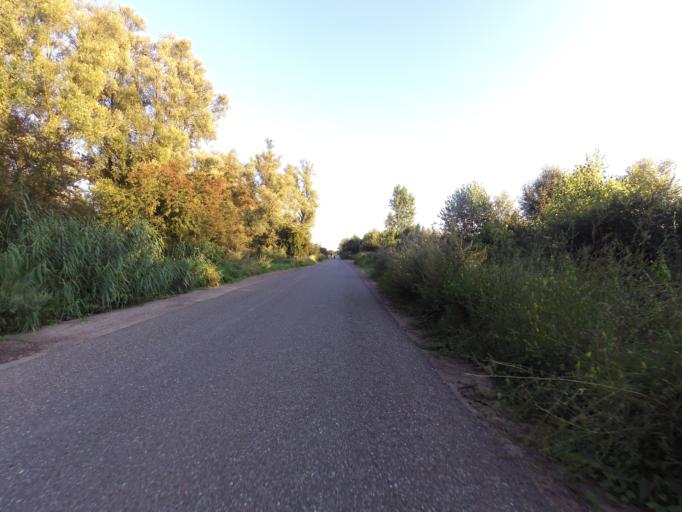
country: NL
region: Gelderland
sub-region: Gemeente Zevenaar
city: Zevenaar
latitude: 51.8814
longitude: 6.0481
